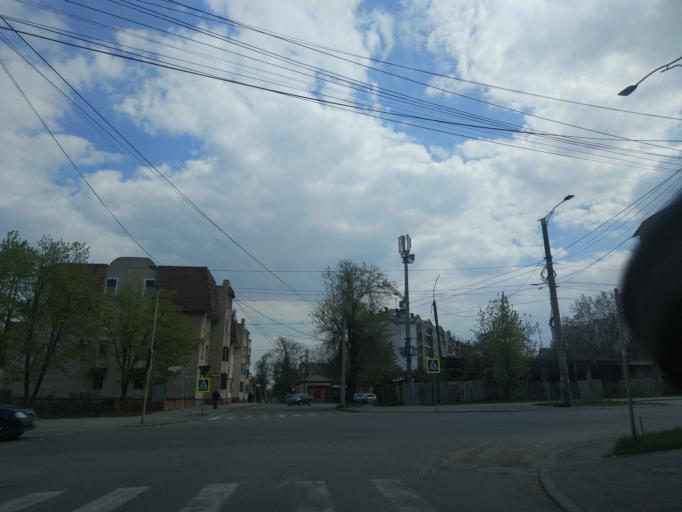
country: MD
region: Chisinau
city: Chisinau
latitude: 47.0265
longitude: 28.8458
